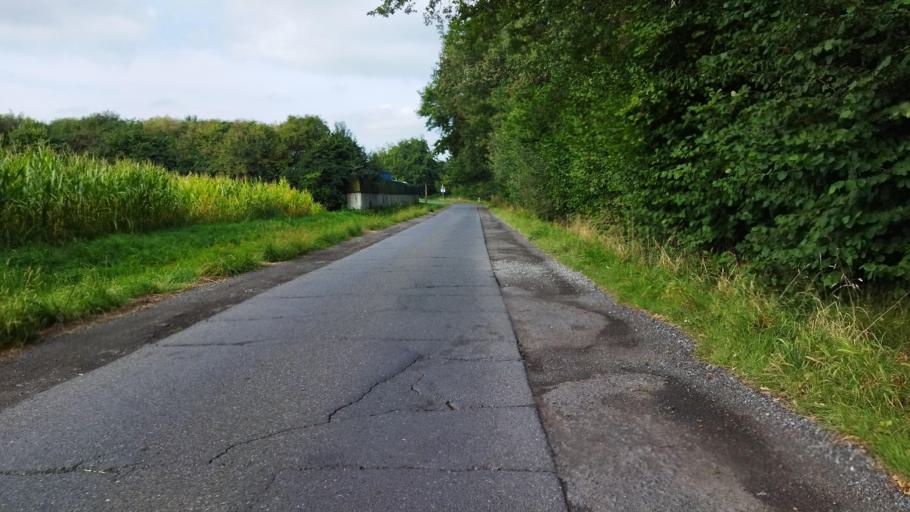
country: DE
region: North Rhine-Westphalia
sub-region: Regierungsbezirk Munster
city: Sassenberg
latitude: 52.0062
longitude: 8.0435
